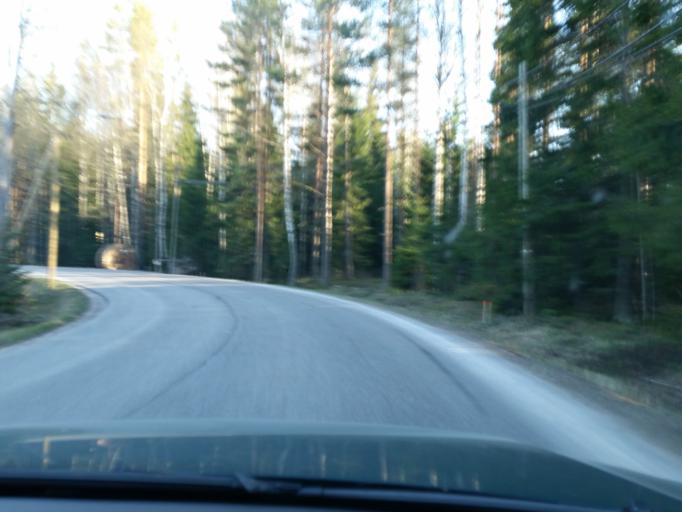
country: FI
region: Uusimaa
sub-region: Helsinki
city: Kirkkonummi
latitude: 60.1260
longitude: 24.5166
